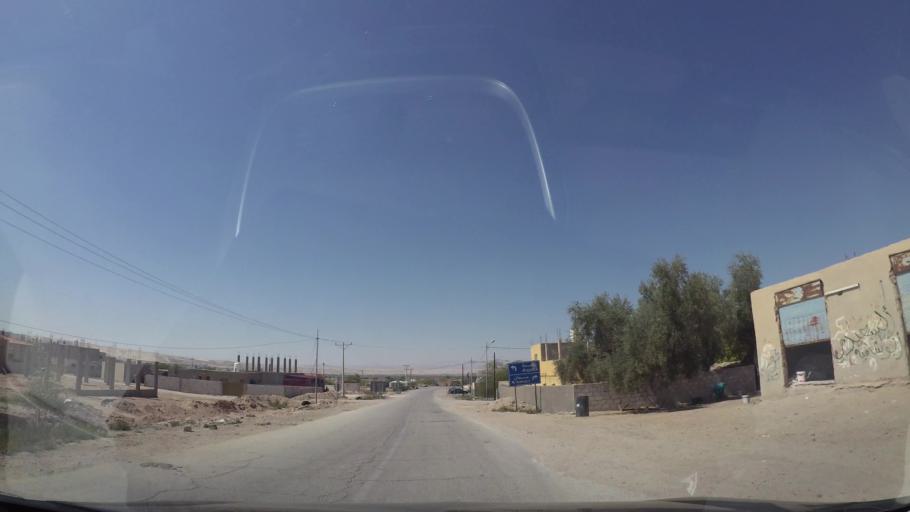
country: JO
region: Karak
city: Safi
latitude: 30.9163
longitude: 35.4599
